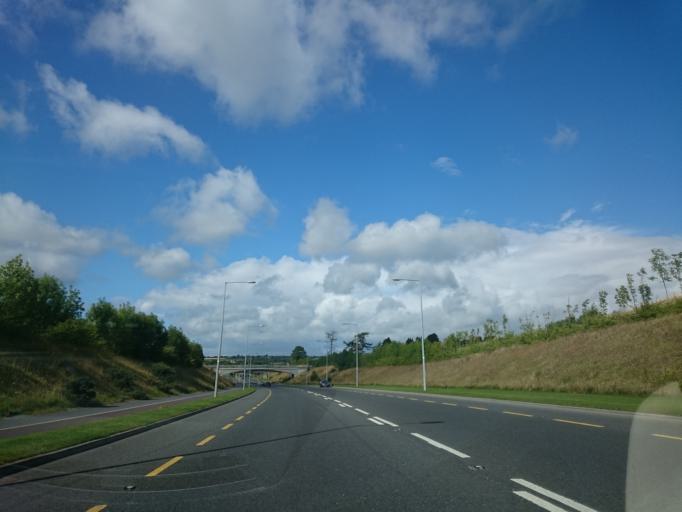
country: IE
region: Leinster
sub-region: Kilkenny
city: Kilkenny
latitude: 52.6768
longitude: -7.2453
